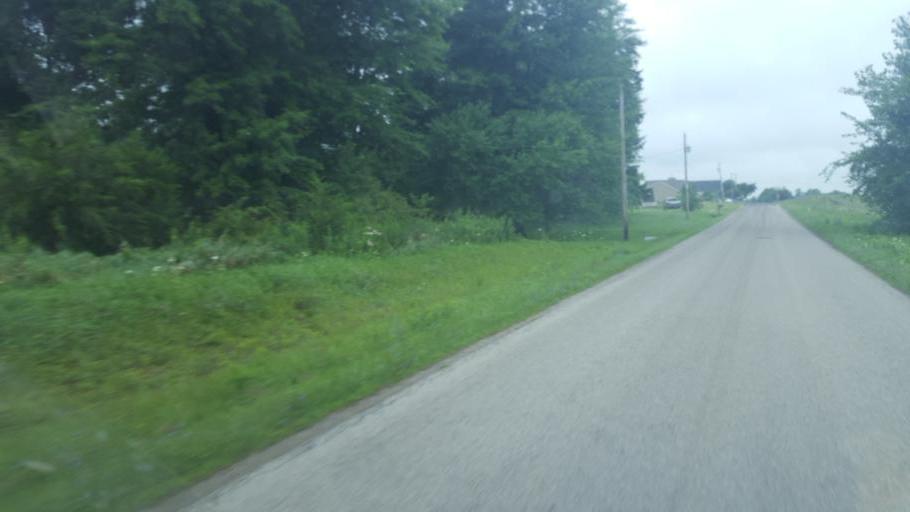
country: US
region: Ohio
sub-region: Knox County
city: Centerburg
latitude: 40.4094
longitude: -82.7660
